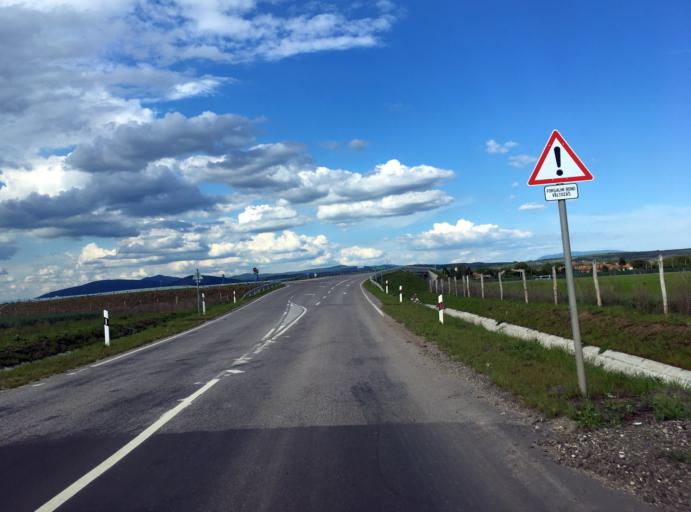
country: HU
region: Heves
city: Lorinci
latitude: 47.7295
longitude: 19.6625
